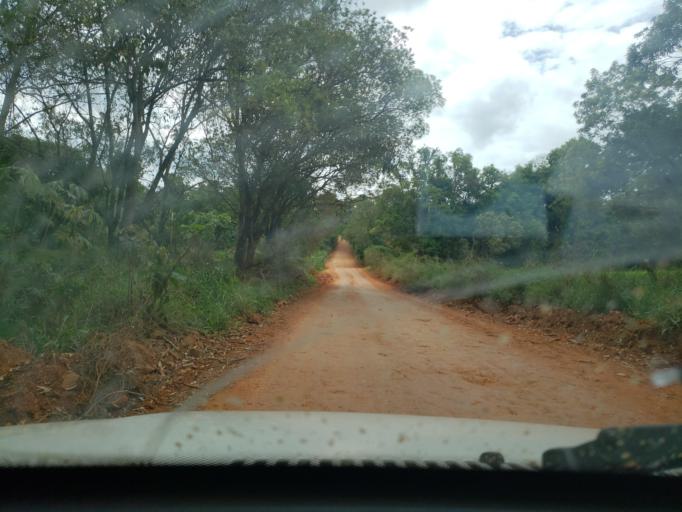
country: BR
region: Minas Gerais
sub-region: Boa Esperanca
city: Boa Esperanca
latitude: -20.9824
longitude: -45.5939
